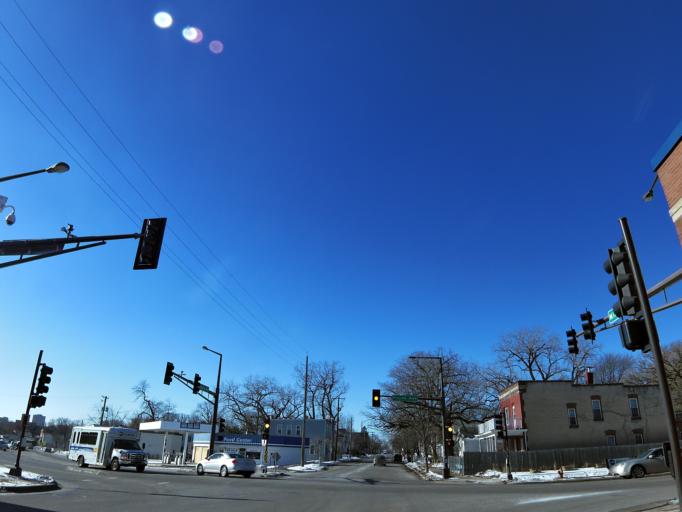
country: US
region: Minnesota
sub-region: Ramsey County
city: Saint Paul
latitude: 44.9631
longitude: -93.0733
